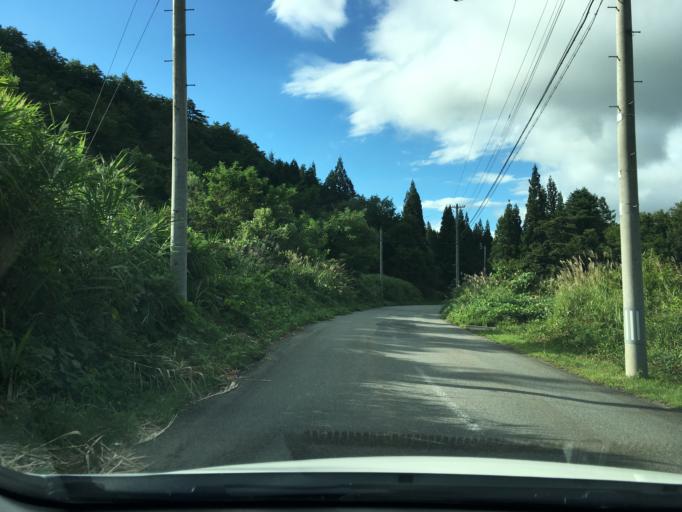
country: JP
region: Yamagata
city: Yonezawa
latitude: 37.9129
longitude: 140.2043
